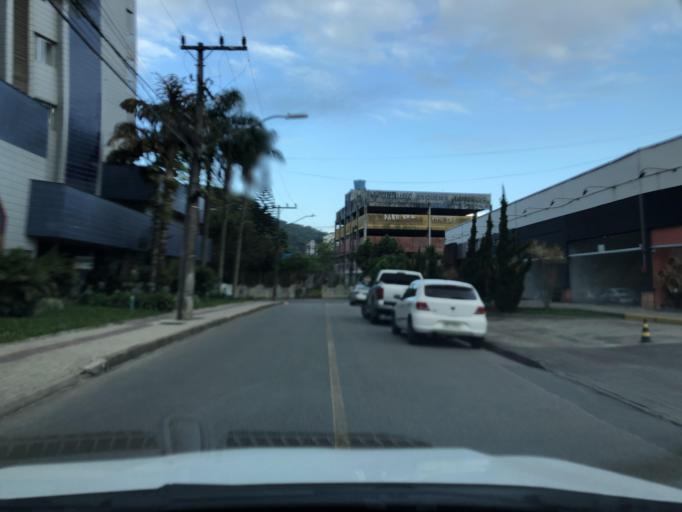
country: BR
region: Santa Catarina
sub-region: Joinville
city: Joinville
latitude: -26.2916
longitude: -48.8462
